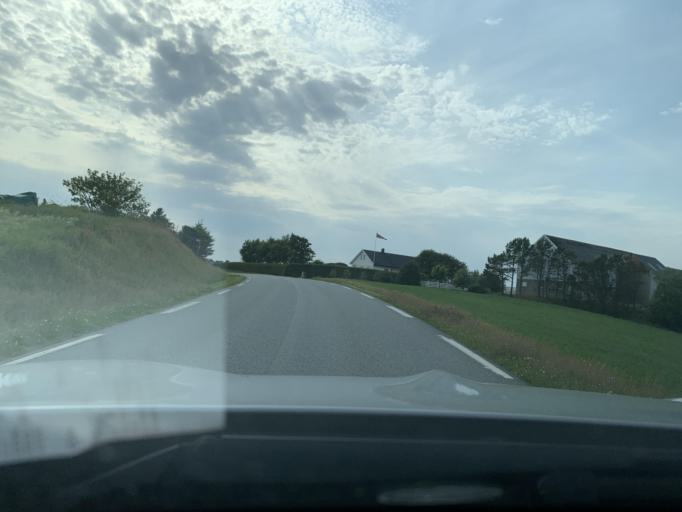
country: NO
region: Rogaland
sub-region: Time
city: Bryne
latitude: 58.7332
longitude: 5.5963
